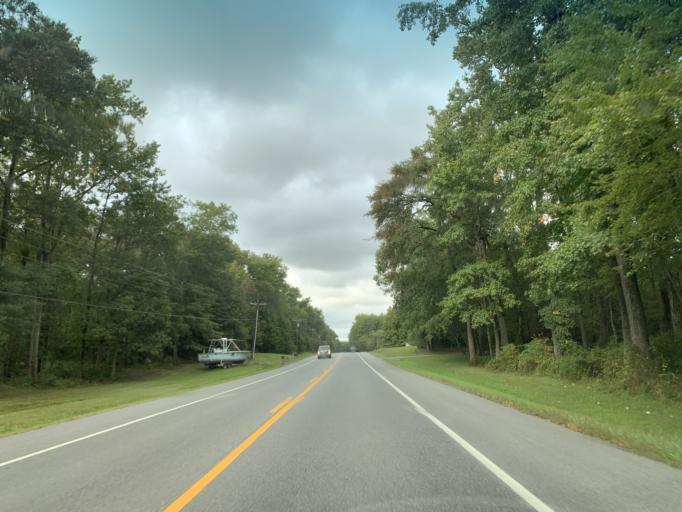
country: US
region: Maryland
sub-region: Caroline County
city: Ridgely
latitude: 39.0132
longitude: -75.8740
